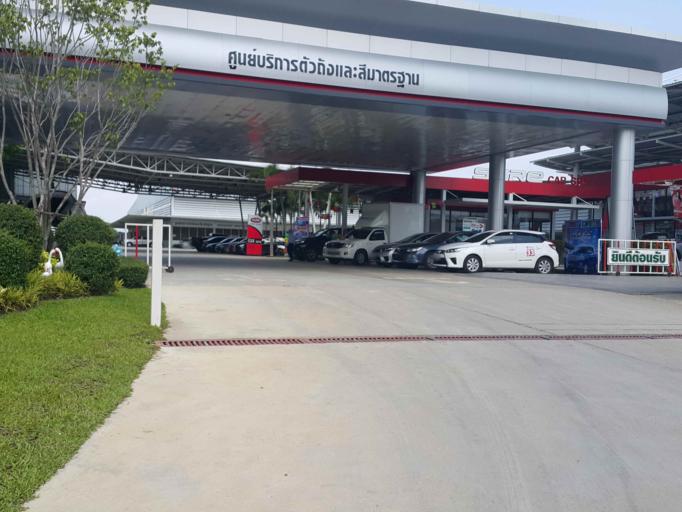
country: TH
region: Chiang Mai
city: San Sai
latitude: 18.8564
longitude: 99.0146
